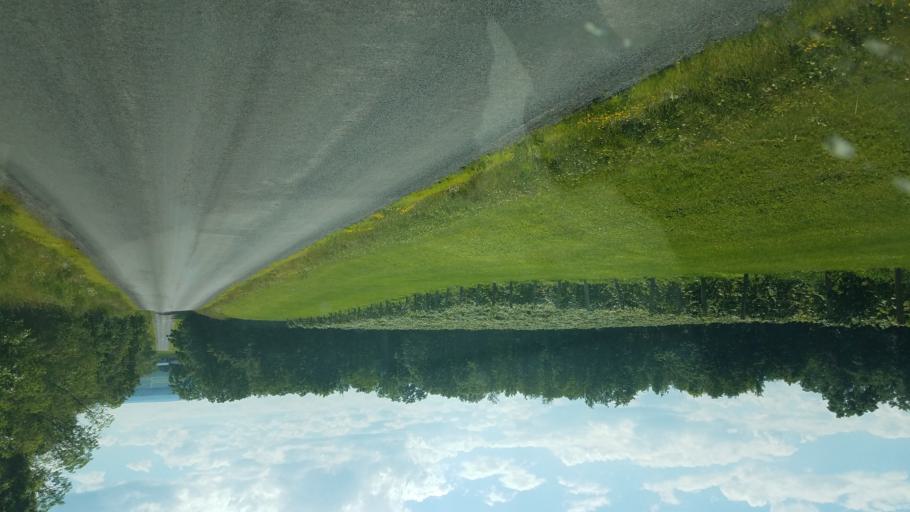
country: US
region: New York
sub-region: Yates County
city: Keuka Park
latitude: 42.5587
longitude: -77.0631
